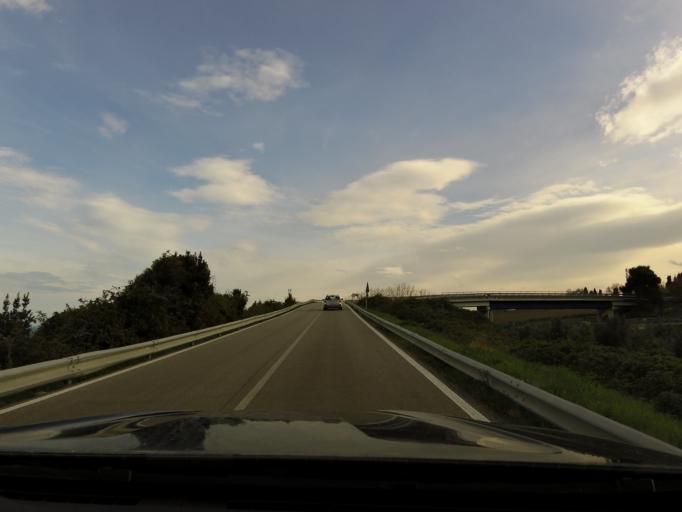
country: IT
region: The Marches
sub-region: Provincia di Macerata
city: Porto Potenza Picena
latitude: 43.3575
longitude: 13.6930
